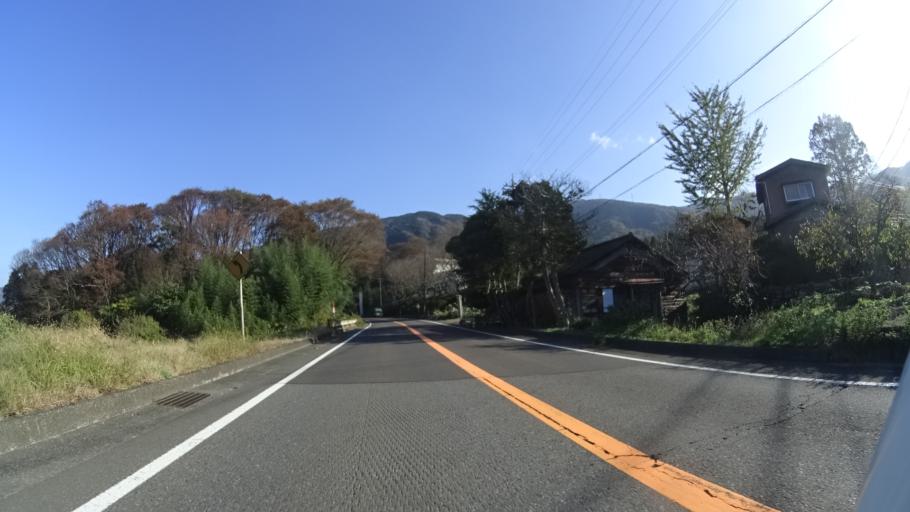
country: JP
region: Fukui
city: Tsuruga
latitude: 35.7373
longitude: 136.0993
